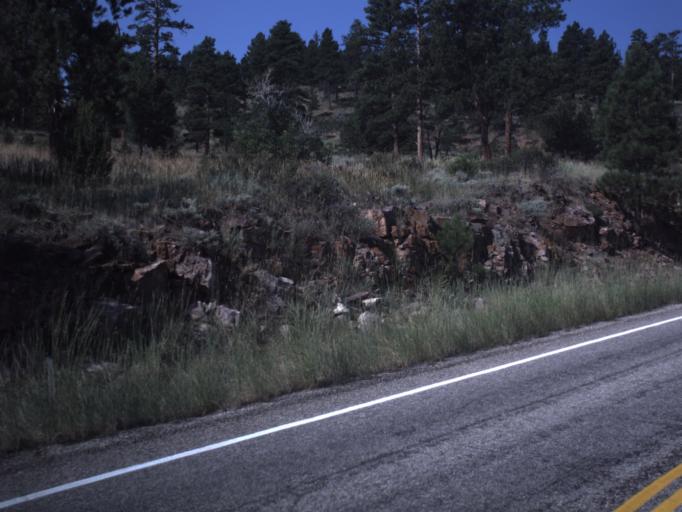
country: US
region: Utah
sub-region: Daggett County
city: Manila
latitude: 40.8964
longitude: -109.4507
